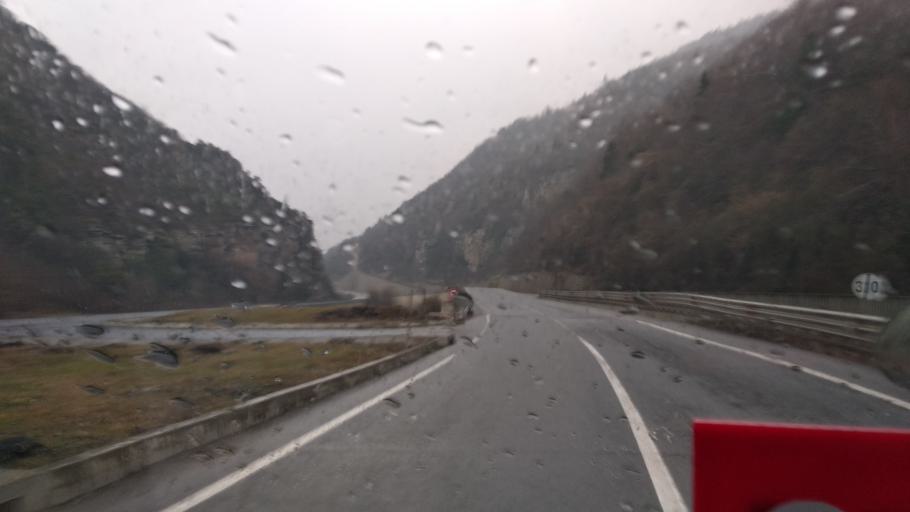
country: TR
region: Trabzon
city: Macka
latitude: 40.8376
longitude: 39.6360
